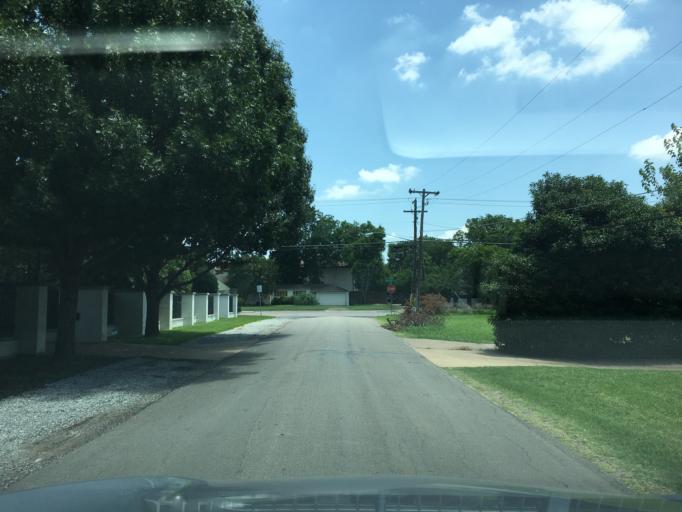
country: US
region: Texas
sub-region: Dallas County
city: University Park
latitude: 32.8839
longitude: -96.8047
